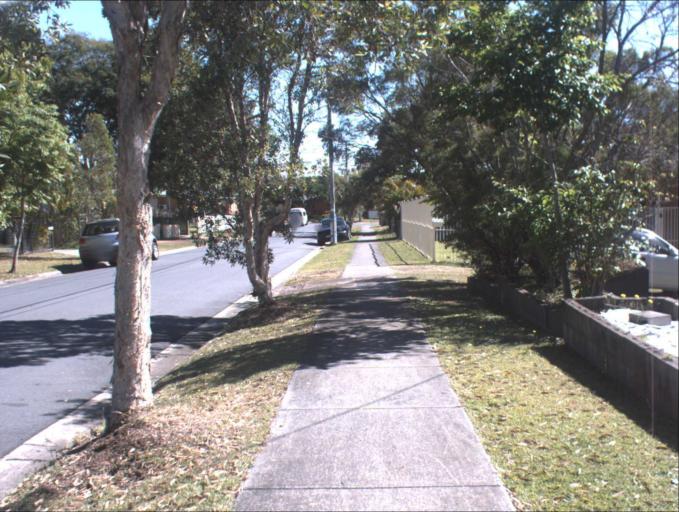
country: AU
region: Queensland
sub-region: Logan
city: Logan City
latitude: -27.6270
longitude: 153.1107
